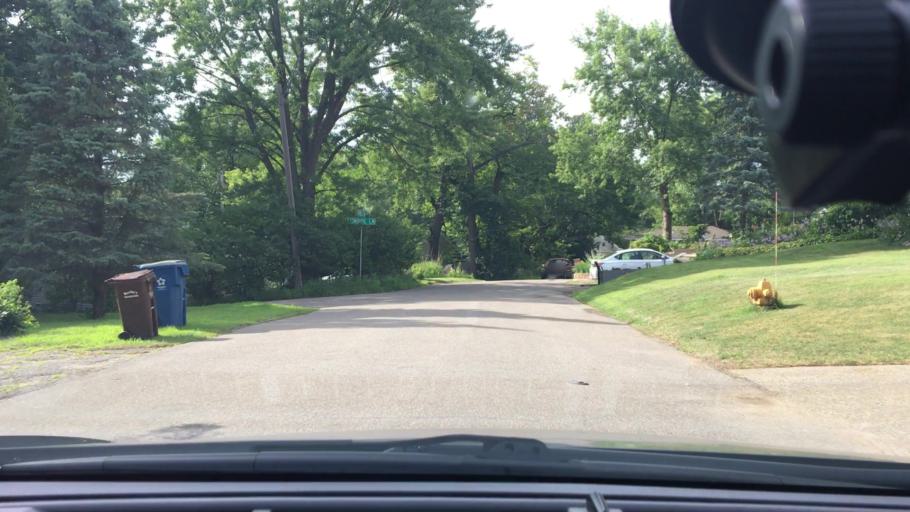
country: US
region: Minnesota
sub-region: Hennepin County
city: Plymouth
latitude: 45.0050
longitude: -93.4330
